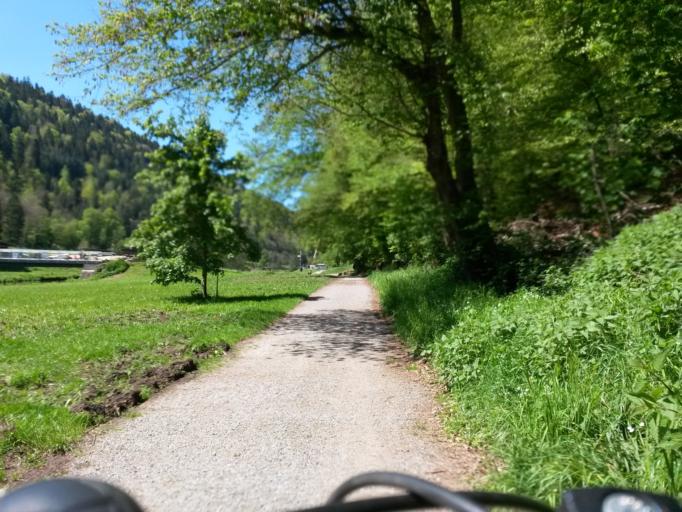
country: DE
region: Baden-Wuerttemberg
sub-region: Karlsruhe Region
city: Unterreichenbach
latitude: 48.8305
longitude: 8.7085
